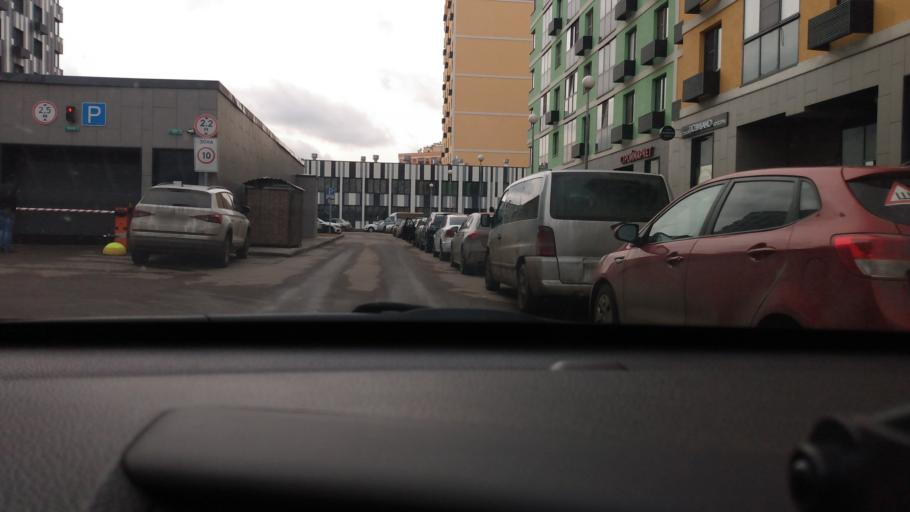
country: RU
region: Moscow
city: Solntsevo
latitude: 55.6436
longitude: 37.3903
